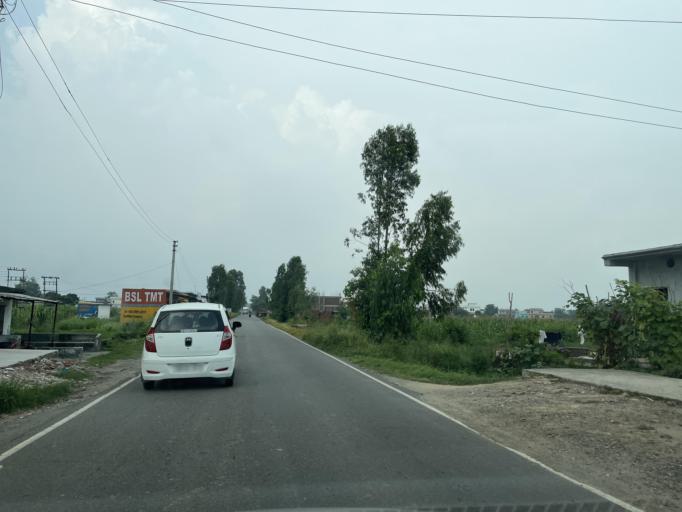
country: IN
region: Uttarakhand
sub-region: Naini Tal
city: Haldwani
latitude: 29.1811
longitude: 79.4738
